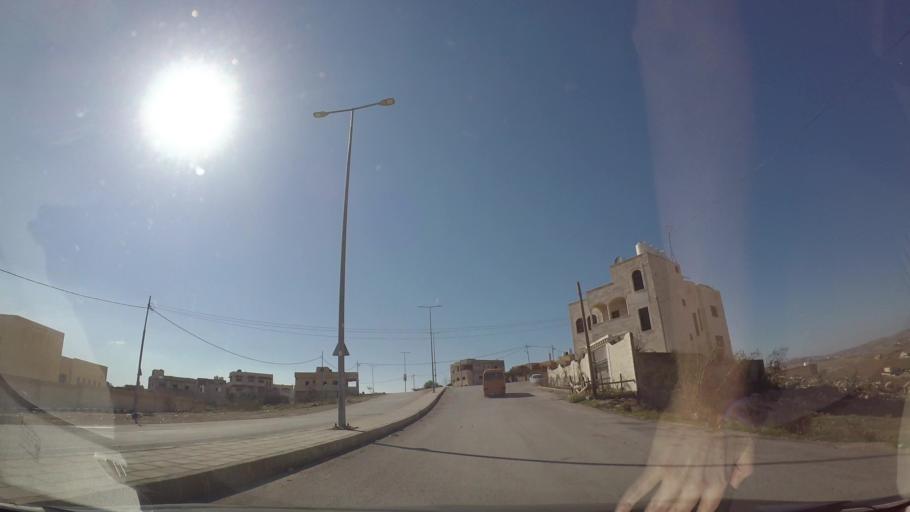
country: JO
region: Zarqa
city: Russeifa
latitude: 32.0427
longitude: 36.0404
